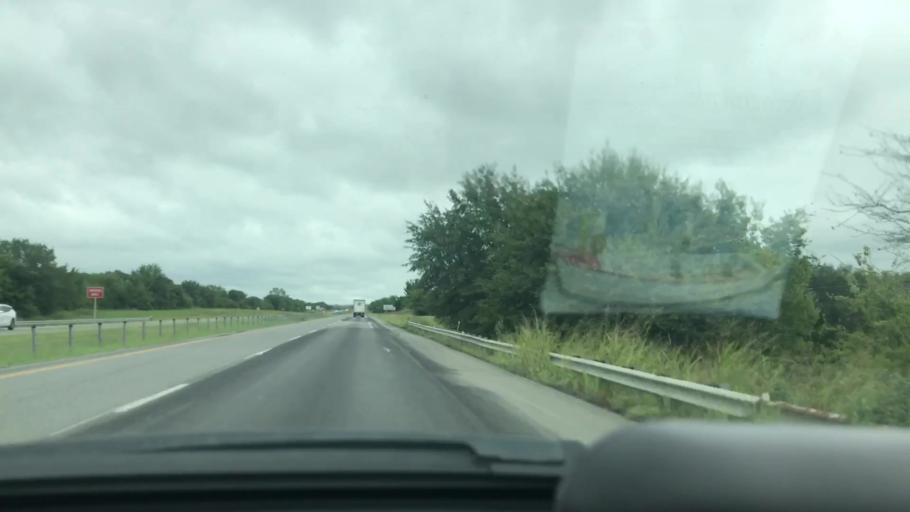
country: US
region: Oklahoma
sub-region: Pittsburg County
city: McAlester
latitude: 34.8004
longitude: -95.8681
